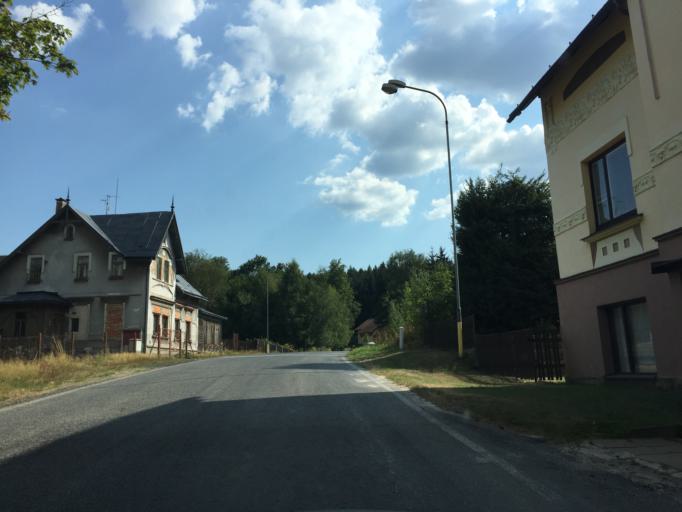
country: CZ
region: Liberecky
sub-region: Okres Jablonec nad Nisou
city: Jablonec nad Nisou
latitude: 50.7171
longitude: 15.1878
